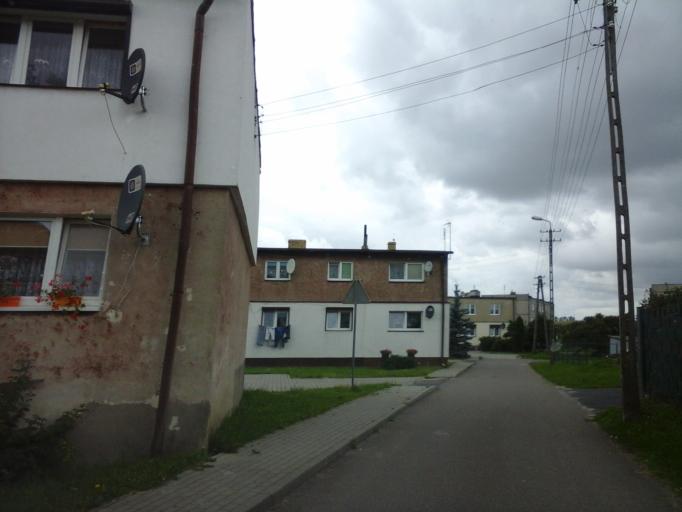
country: PL
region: West Pomeranian Voivodeship
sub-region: Powiat choszczenski
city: Krzecin
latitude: 53.0023
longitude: 15.4171
